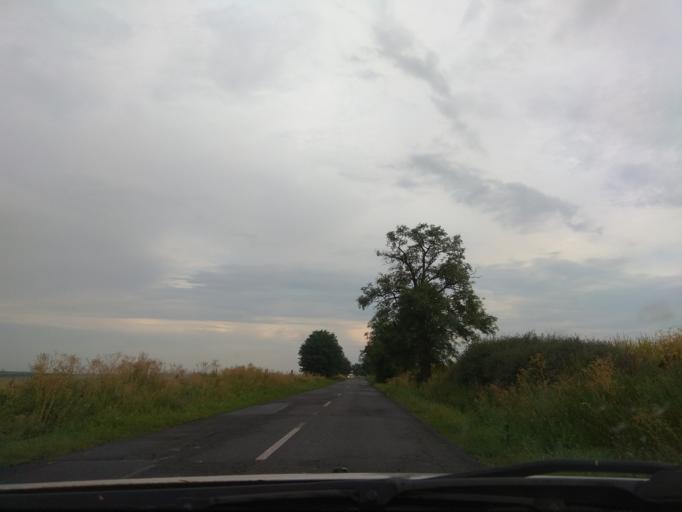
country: HU
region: Borsod-Abauj-Zemplen
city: Gesztely
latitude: 48.1377
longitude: 20.9736
